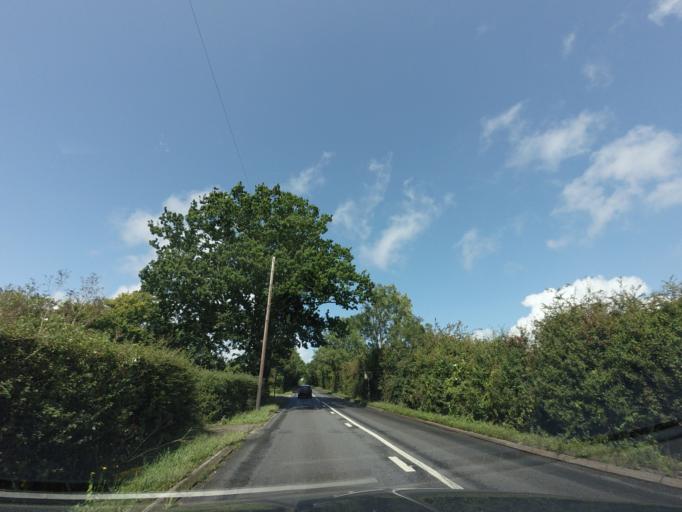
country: GB
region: England
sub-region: Kent
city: East Peckham
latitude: 51.2345
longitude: 0.3831
